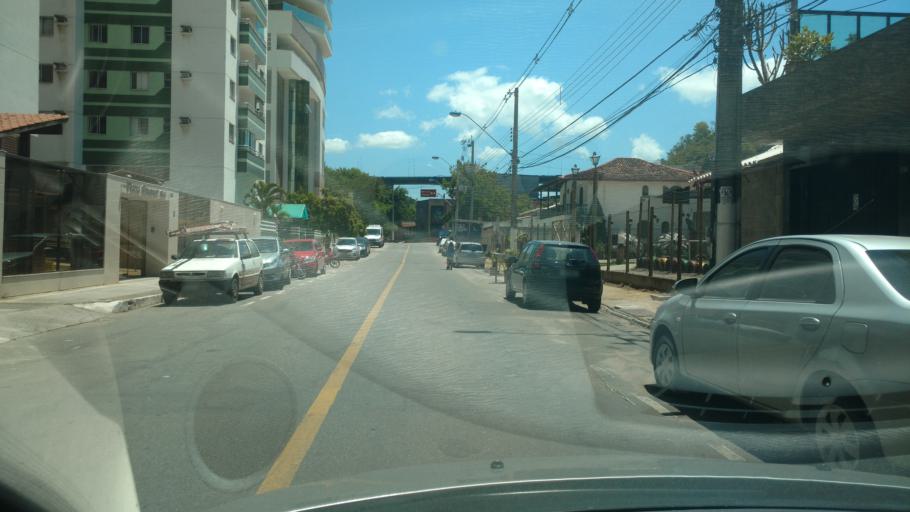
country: BR
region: Espirito Santo
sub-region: Vila Velha
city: Vila Velha
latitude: -20.3296
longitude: -40.2795
